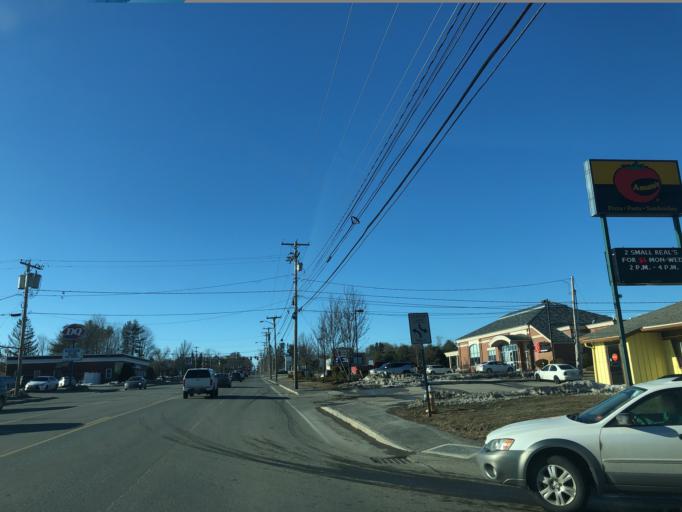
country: US
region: Maine
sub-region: Penobscot County
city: Bangor
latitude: 44.8230
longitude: -68.7788
